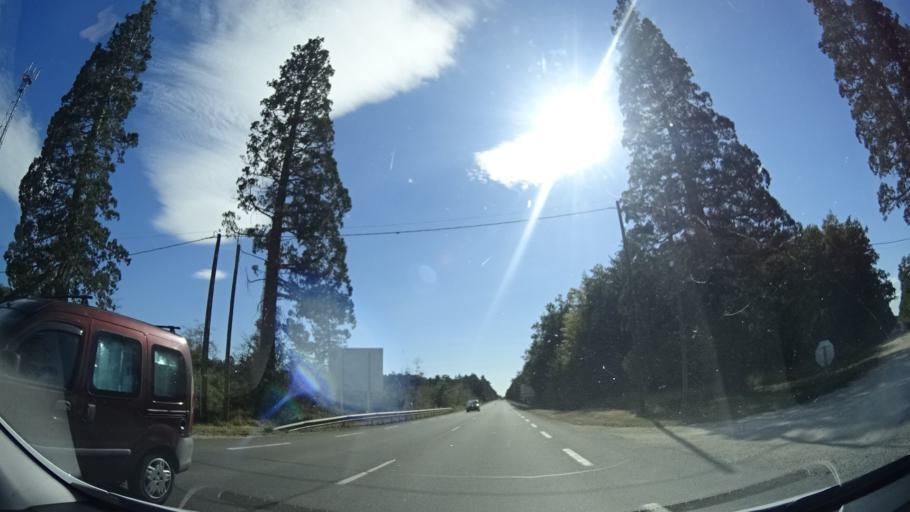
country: FR
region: Centre
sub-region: Departement du Loiret
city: Vitry-aux-Loges
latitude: 47.9138
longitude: 2.3087
